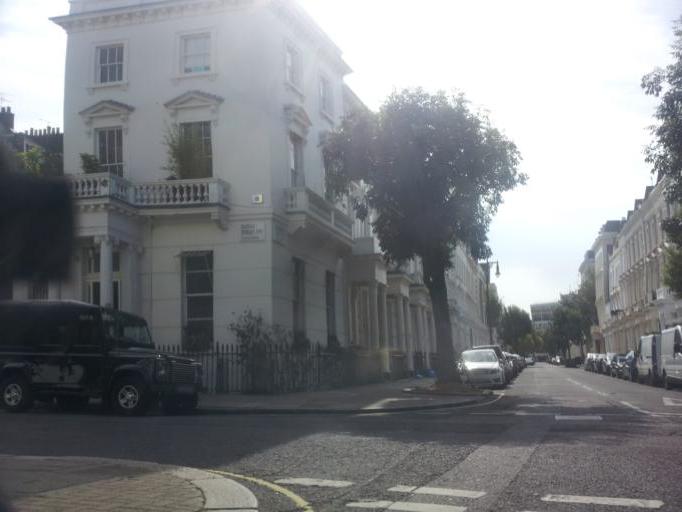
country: GB
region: England
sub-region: Greater London
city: Battersea
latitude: 51.4897
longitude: -0.1434
